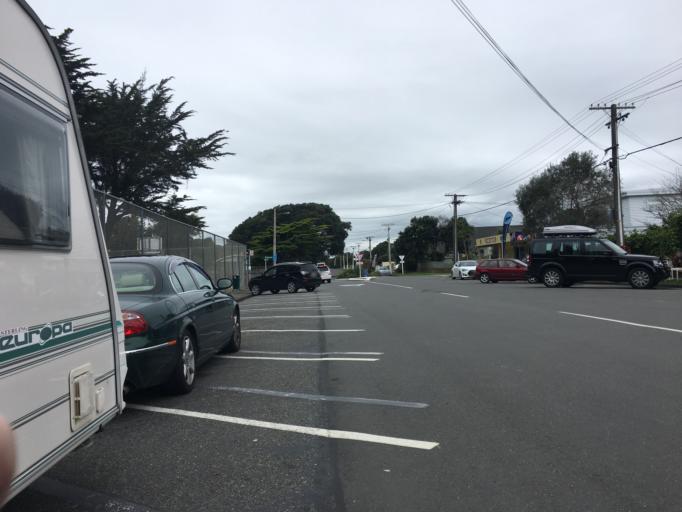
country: NZ
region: Wellington
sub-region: Kapiti Coast District
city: Paraparaumu
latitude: -40.8615
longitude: 175.0241
